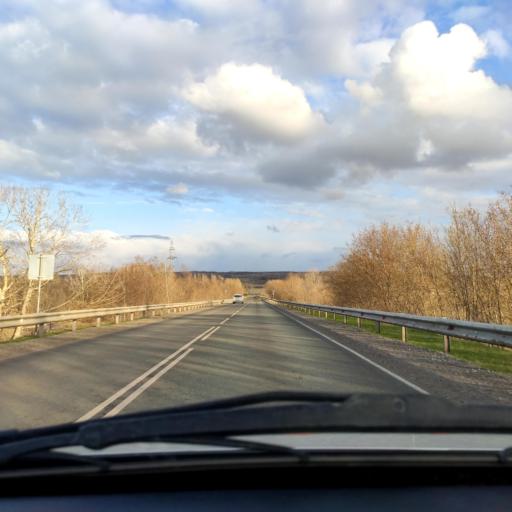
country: RU
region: Bashkortostan
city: Chishmy
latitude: 54.5687
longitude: 55.4681
